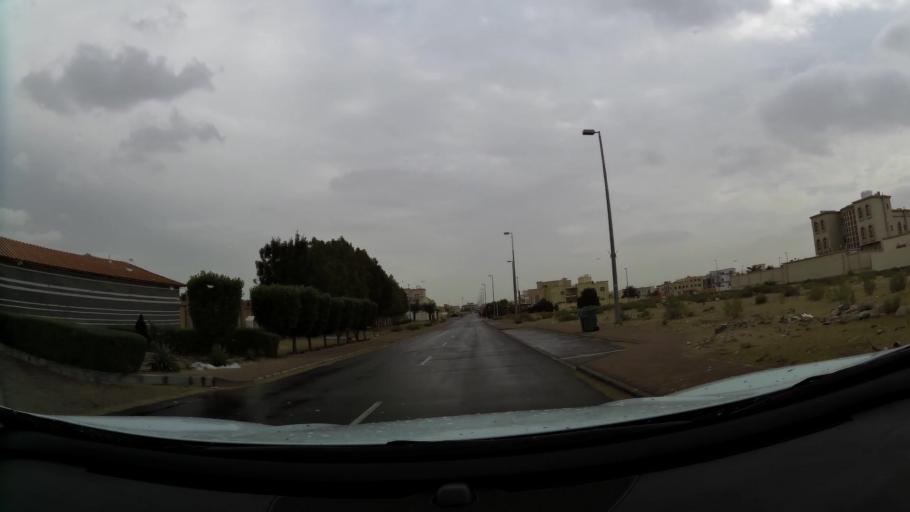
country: AE
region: Abu Dhabi
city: Abu Dhabi
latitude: 24.3624
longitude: 54.6237
